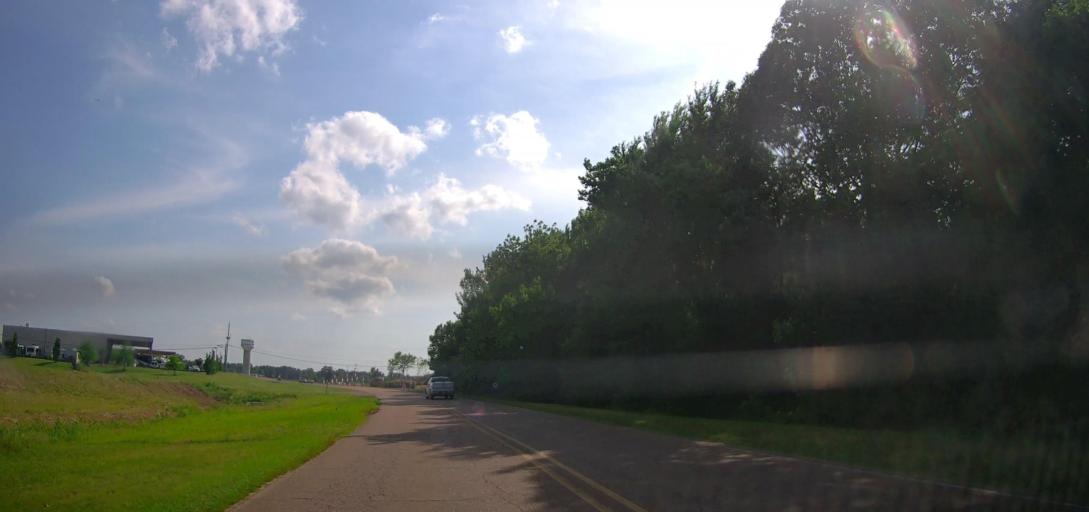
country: US
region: Mississippi
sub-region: De Soto County
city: Olive Branch
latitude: 34.9808
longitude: -89.8619
